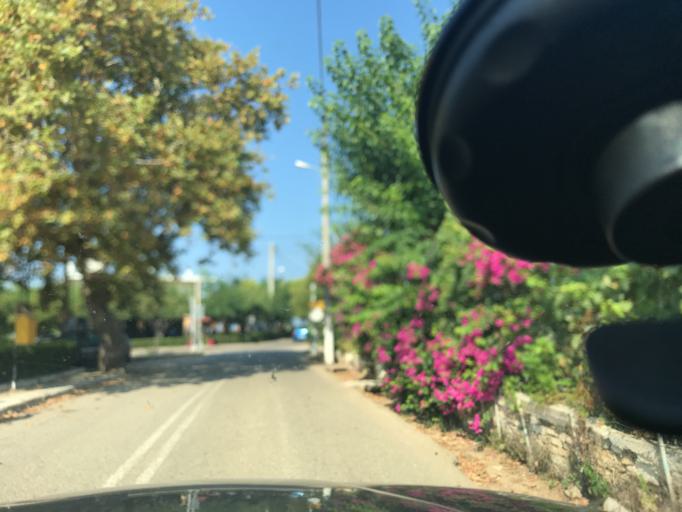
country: GR
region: West Greece
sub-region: Nomos Ileias
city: Kardamas
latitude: 37.7192
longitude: 21.3199
